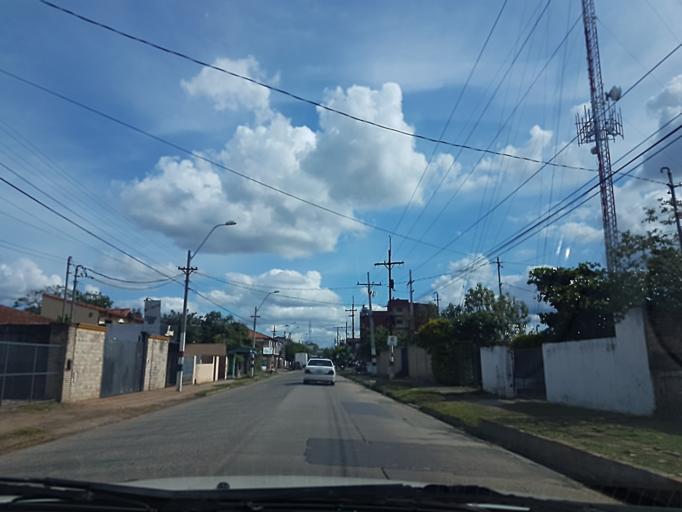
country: PY
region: Central
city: Colonia Mariano Roque Alonso
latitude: -25.2077
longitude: -57.5332
